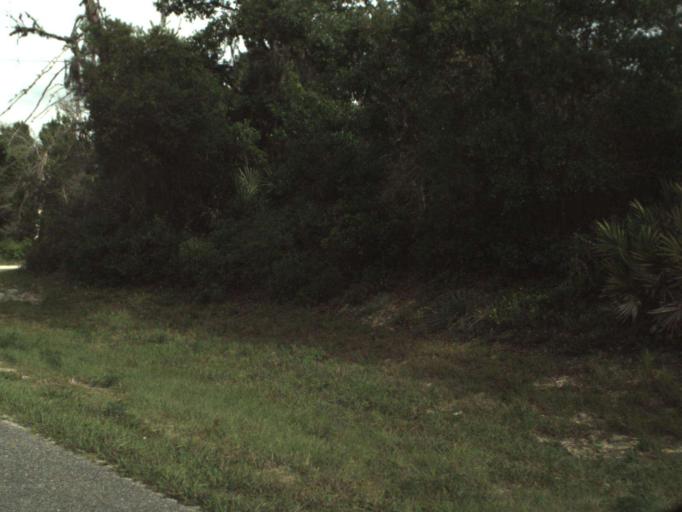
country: US
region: Florida
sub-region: Seminole County
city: Geneva
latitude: 28.7242
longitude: -81.0930
